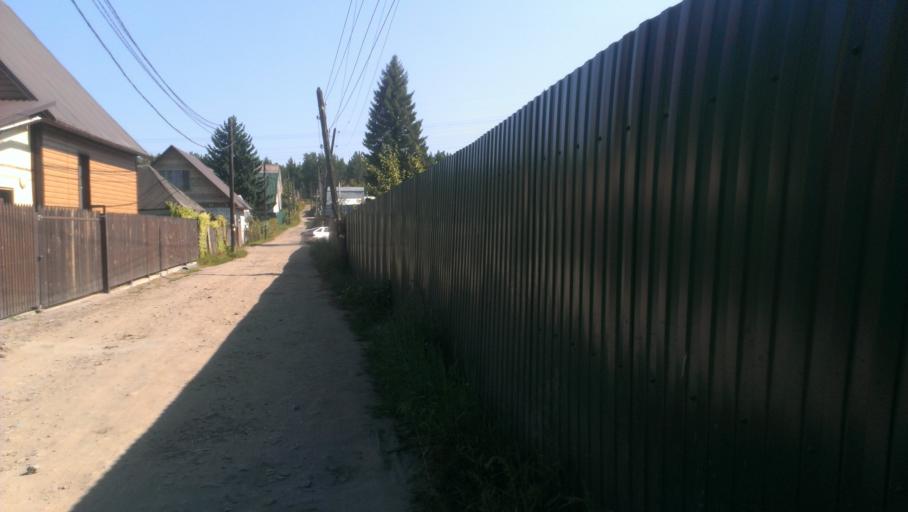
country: RU
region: Altai Krai
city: Novosilikatnyy
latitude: 53.3219
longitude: 83.6832
